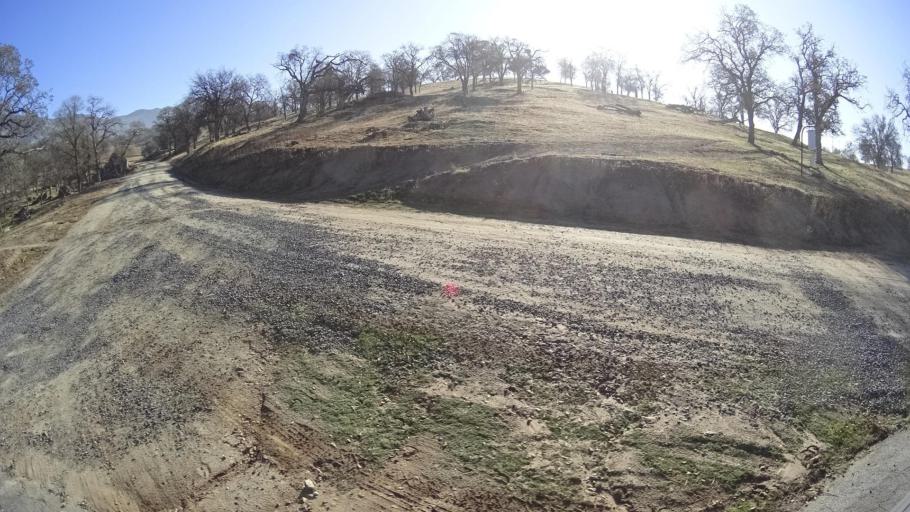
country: US
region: California
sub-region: Kern County
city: Alta Sierra
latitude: 35.7421
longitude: -118.8192
